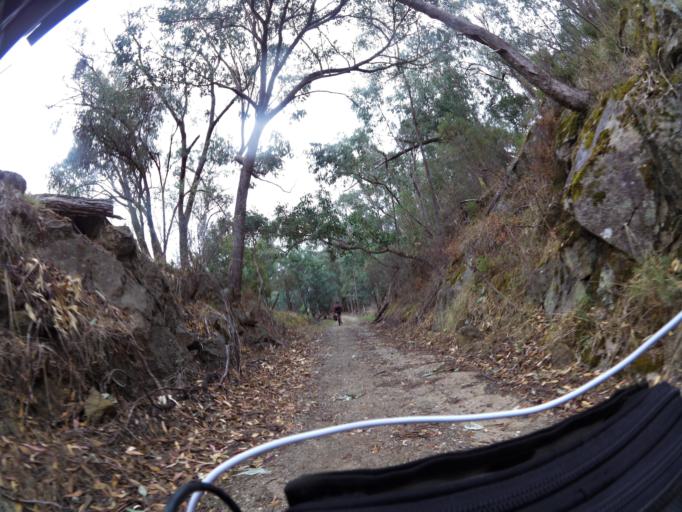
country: AU
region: New South Wales
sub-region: Greater Hume Shire
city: Holbrook
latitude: -36.1711
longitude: 147.4042
